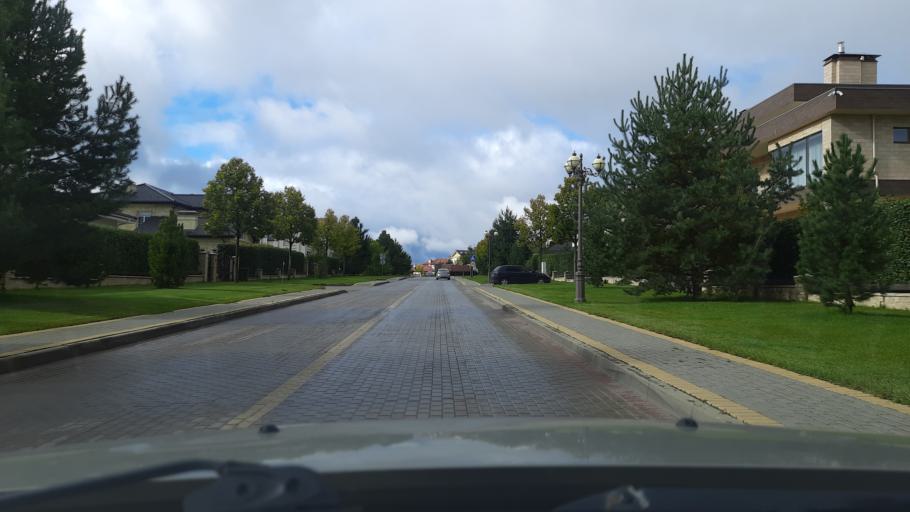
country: RU
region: Moskovskaya
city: Nikolina Gora
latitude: 55.7744
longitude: 37.0498
